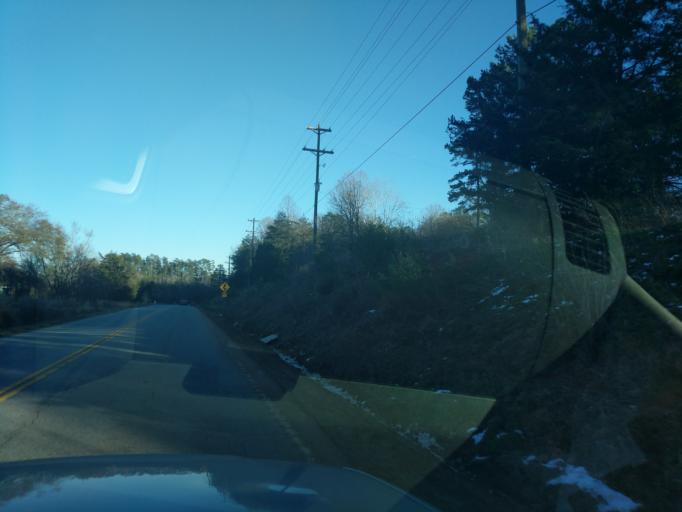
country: US
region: South Carolina
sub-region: Oconee County
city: Westminster
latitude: 34.6882
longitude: -83.1660
